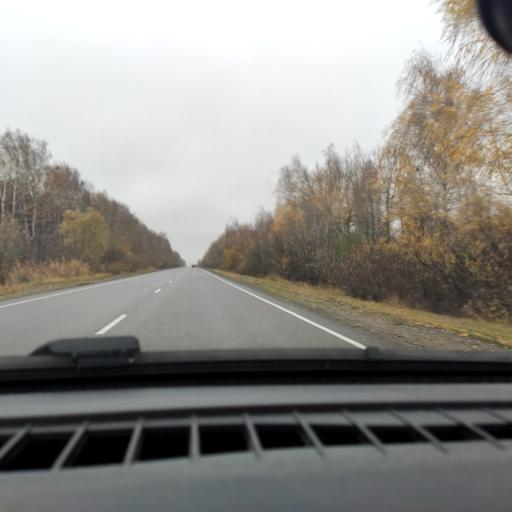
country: RU
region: Voronezj
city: Kolodeznyy
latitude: 51.3549
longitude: 39.0237
